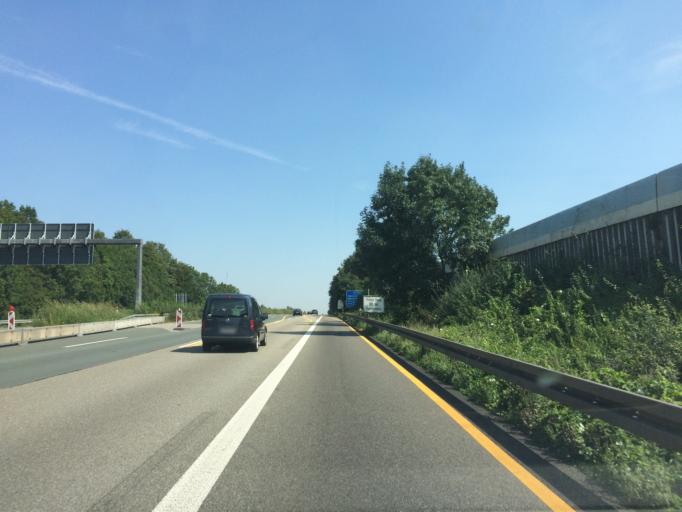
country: DE
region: North Rhine-Westphalia
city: Bergkamen
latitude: 51.5951
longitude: 7.6308
